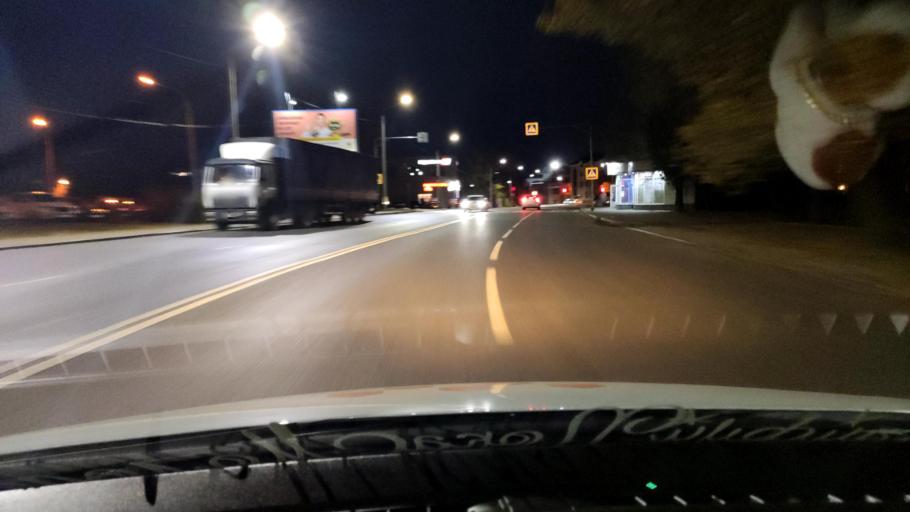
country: RU
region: Voronezj
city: Voronezh
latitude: 51.6846
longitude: 39.2025
